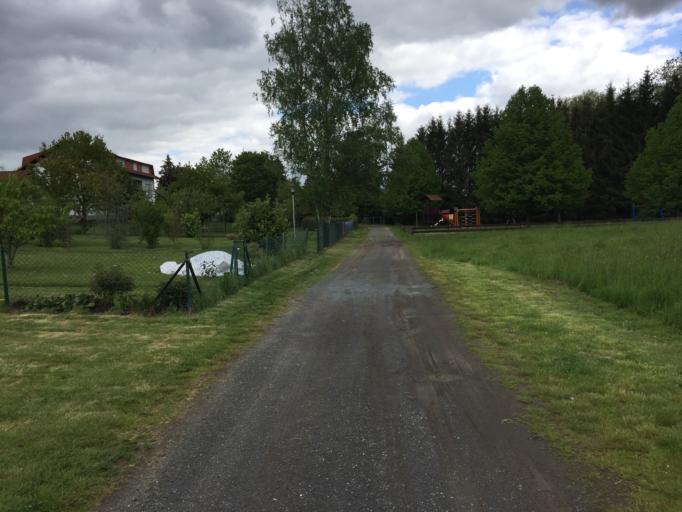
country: DE
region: Hesse
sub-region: Regierungsbezirk Giessen
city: Grunberg
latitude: 50.5739
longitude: 8.9315
